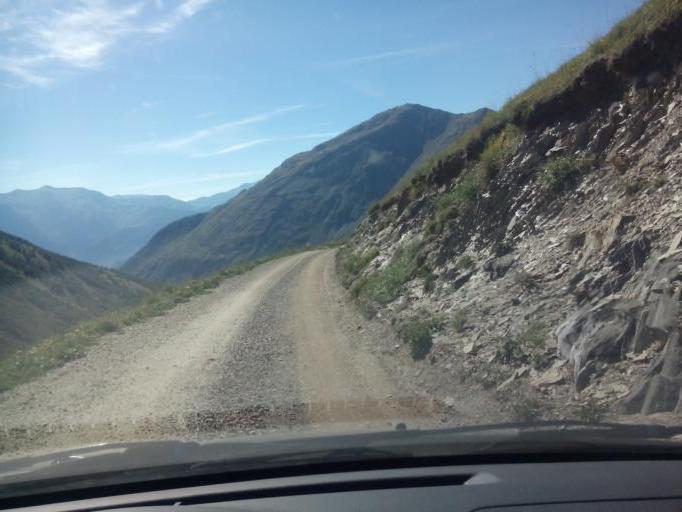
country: FR
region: Rhone-Alpes
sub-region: Departement de l'Isere
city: Mont-de-Lans
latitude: 45.0726
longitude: 6.1836
